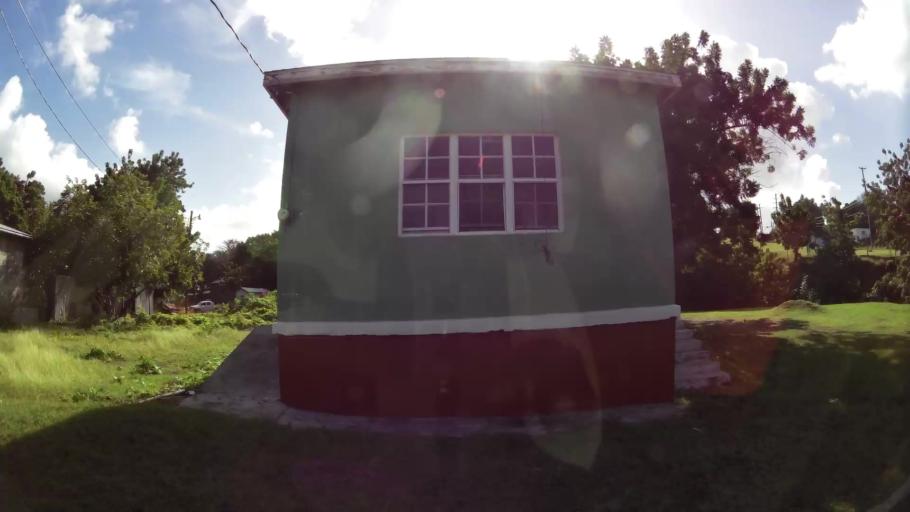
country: KN
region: Saint Paul Charlestown
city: Charlestown
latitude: 17.1326
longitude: -62.6271
